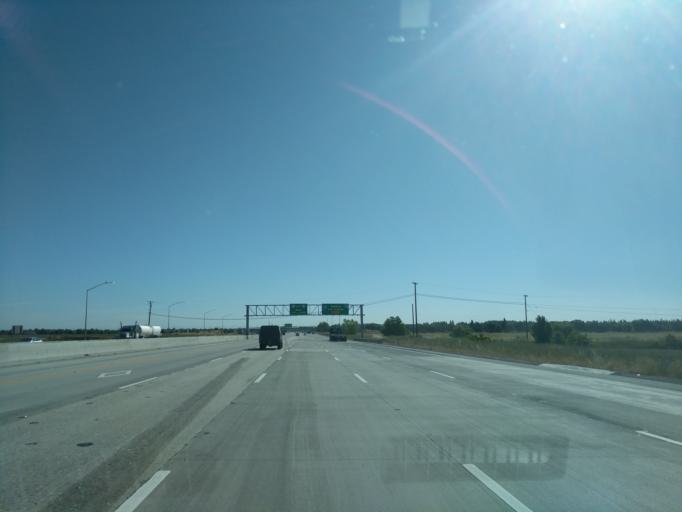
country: US
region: California
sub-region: Yolo County
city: West Sacramento
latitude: 38.6171
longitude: -121.5317
